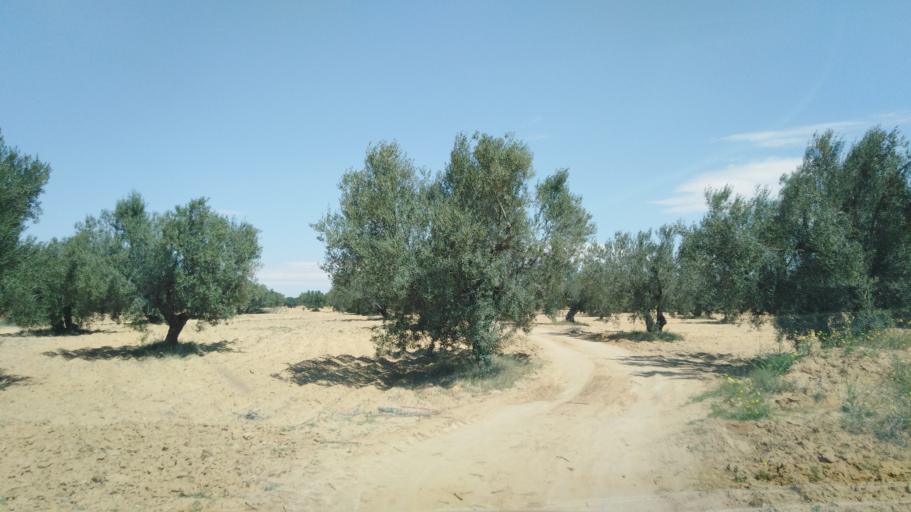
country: TN
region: Safaqis
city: Sfax
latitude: 34.7827
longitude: 10.5278
